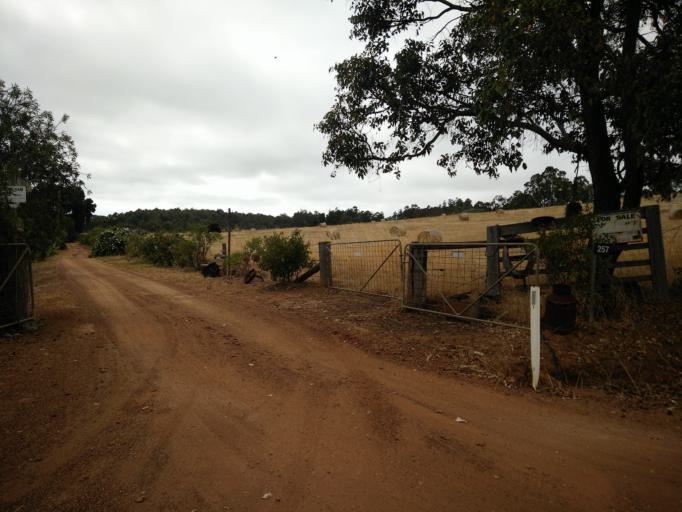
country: AU
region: Western Australia
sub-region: Bridgetown-Greenbushes
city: Bridgetown
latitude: -33.9552
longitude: 116.1696
